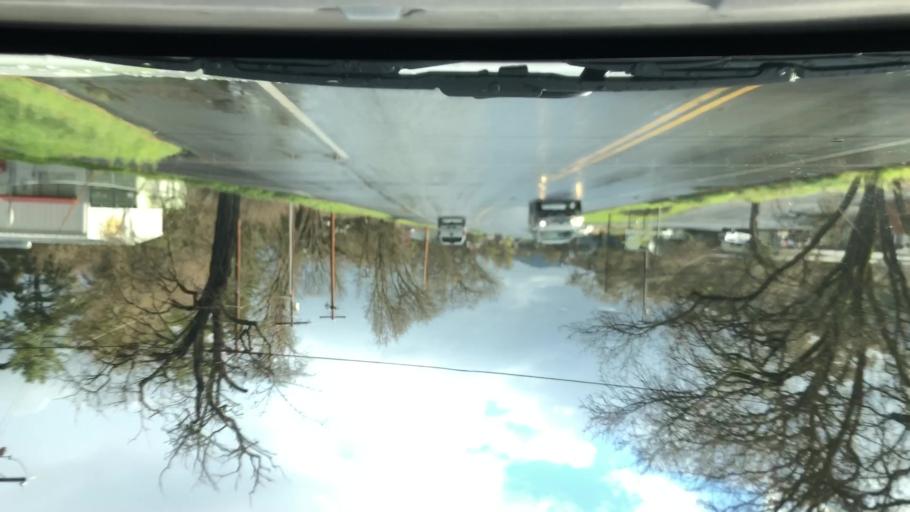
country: US
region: California
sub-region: Mendocino County
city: Ukiah
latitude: 39.1165
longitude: -123.1999
